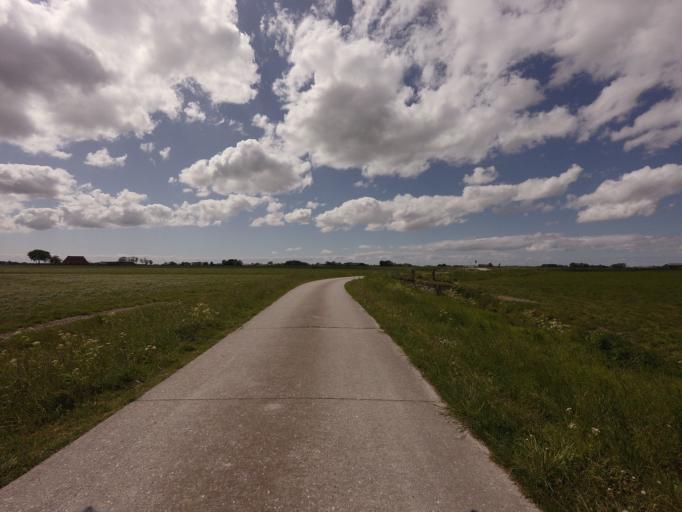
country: NL
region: Friesland
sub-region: Gemeente Franekeradeel
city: Tzum
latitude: 53.1292
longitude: 5.5582
